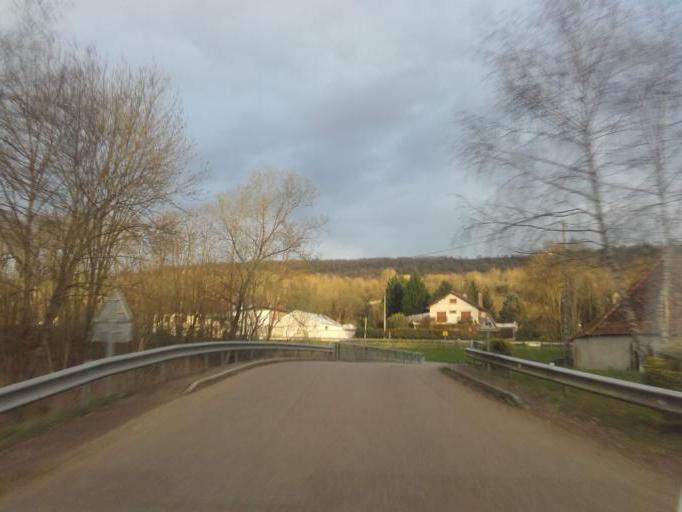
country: FR
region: Bourgogne
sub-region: Departement de Saone-et-Loire
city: Saint-Leger-sur-Dheune
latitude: 46.8914
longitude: 4.6796
